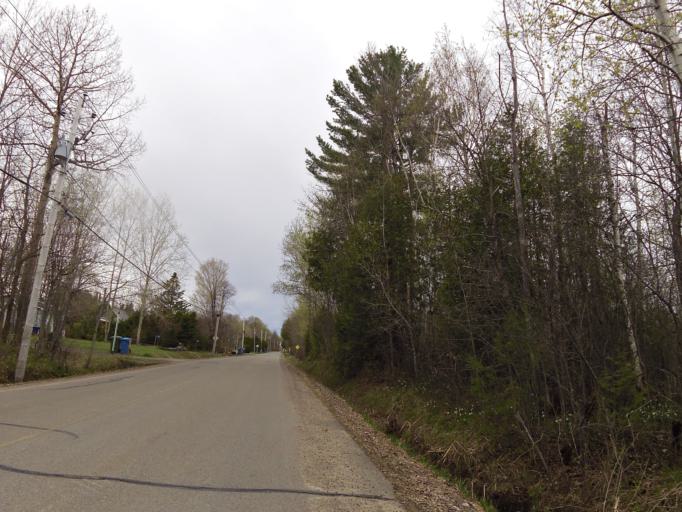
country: CA
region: Ontario
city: Hawkesbury
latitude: 45.6229
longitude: -74.5631
